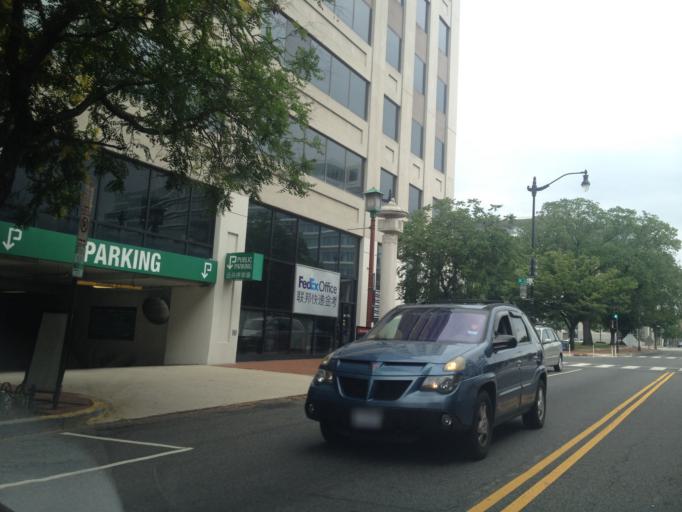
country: US
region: Washington, D.C.
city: Washington, D.C.
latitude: 38.9016
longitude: -77.0219
